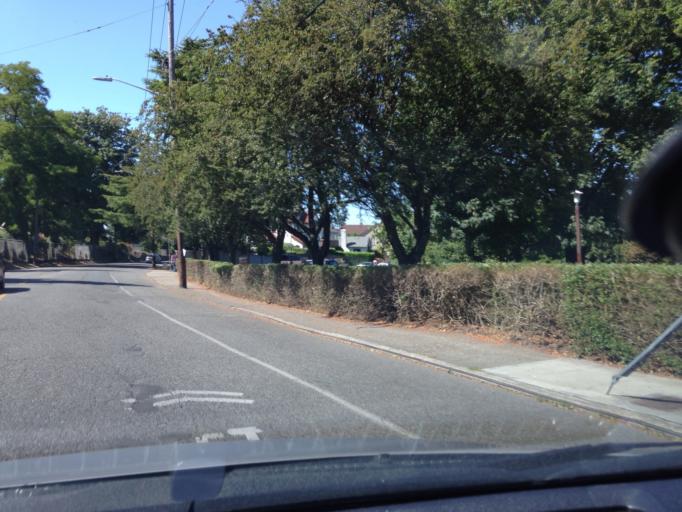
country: US
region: Washington
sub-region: King County
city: Seattle
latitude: 47.6342
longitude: -122.3127
